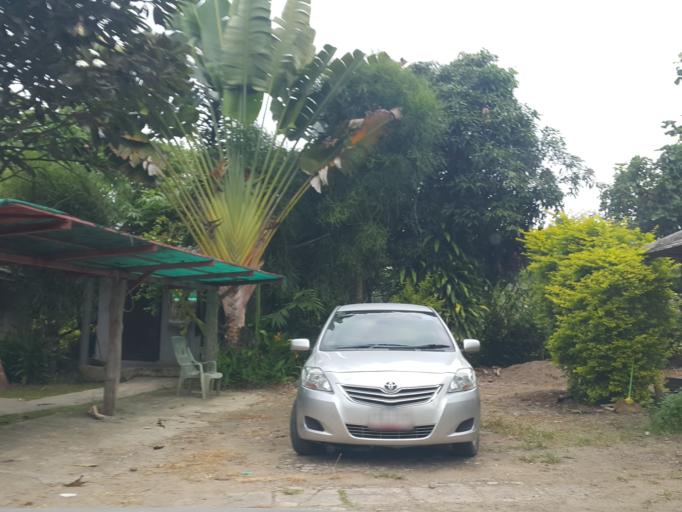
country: TH
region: Chiang Mai
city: Pai
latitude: 19.3593
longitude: 98.4488
